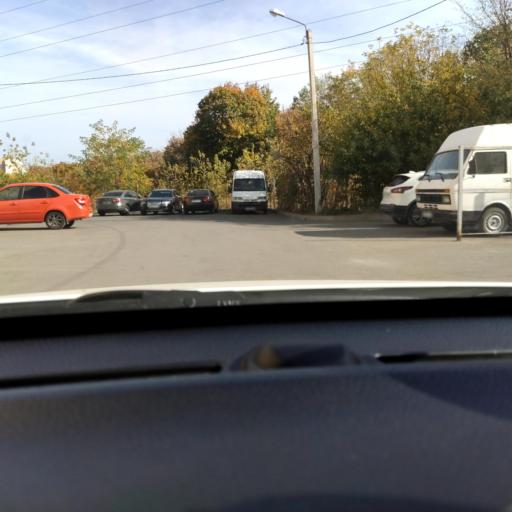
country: RU
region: Voronezj
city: Voronezh
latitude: 51.7018
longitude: 39.2074
